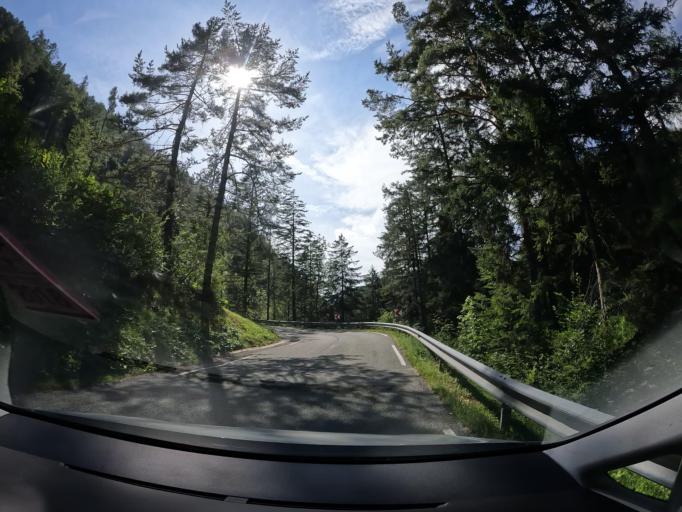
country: AT
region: Carinthia
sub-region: Politischer Bezirk Klagenfurt Land
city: Ludmannsdorf
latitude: 46.5218
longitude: 14.0956
